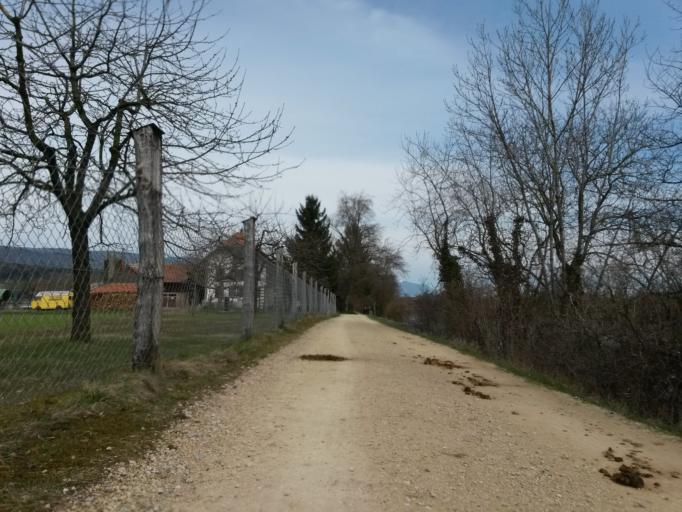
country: CH
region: Bern
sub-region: Biel/Bienne District
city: Orpund
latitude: 47.1311
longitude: 7.3023
